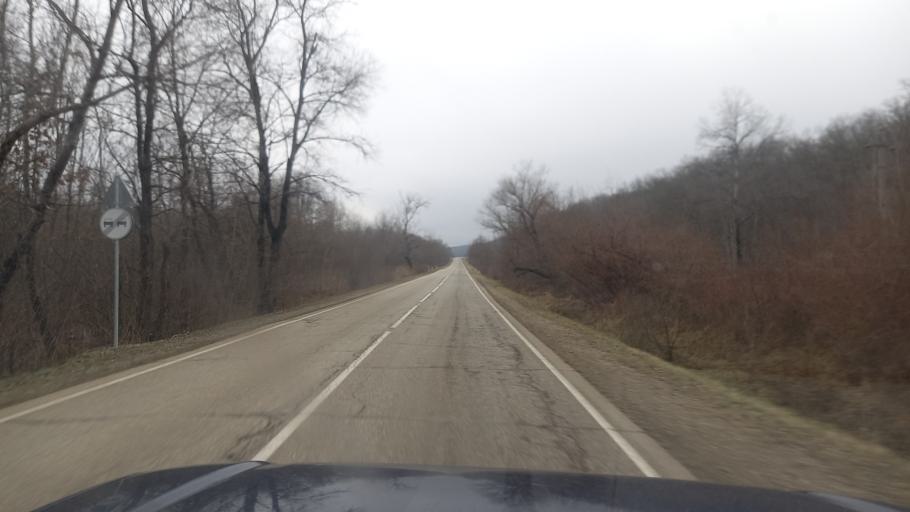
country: RU
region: Krasnodarskiy
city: Neftegorsk
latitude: 44.2811
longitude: 39.7977
